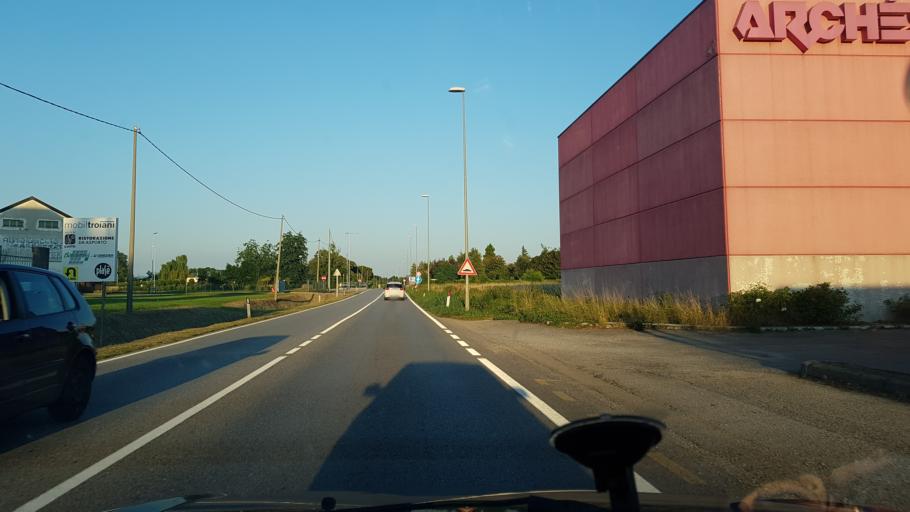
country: IT
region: Friuli Venezia Giulia
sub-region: Provincia di Udine
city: Martignacco
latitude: 46.0883
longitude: 13.1512
